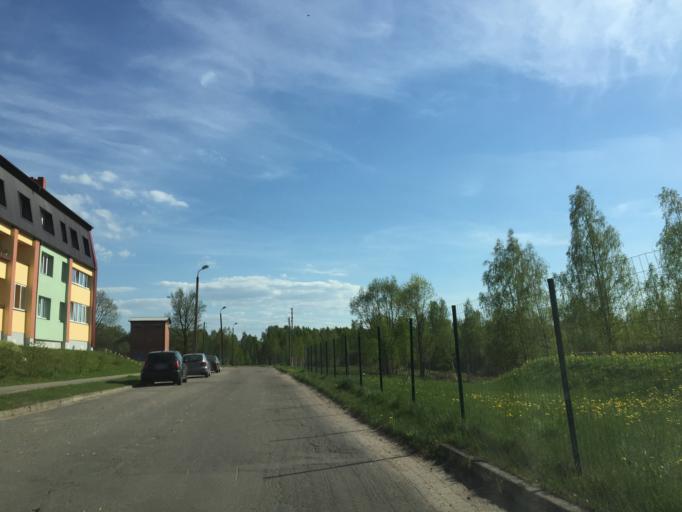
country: LV
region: Limbazu Rajons
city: Limbazi
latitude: 57.5093
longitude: 24.7055
